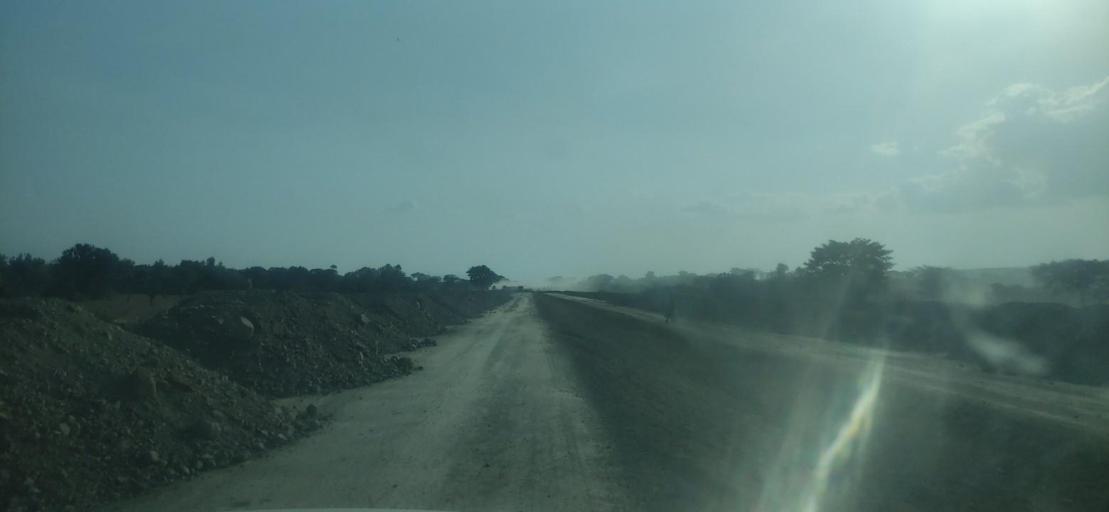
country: ET
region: Southern Nations, Nationalities, and People's Region
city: Hawassa
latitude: 7.1605
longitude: 38.4828
